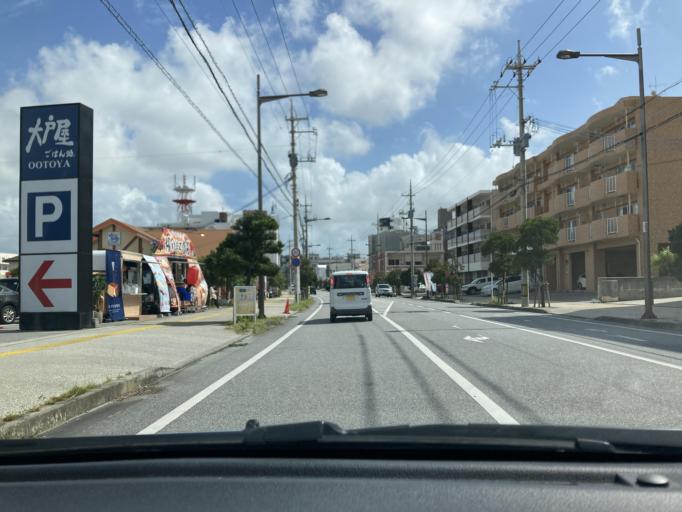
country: JP
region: Okinawa
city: Ginowan
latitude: 26.2708
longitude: 127.7313
